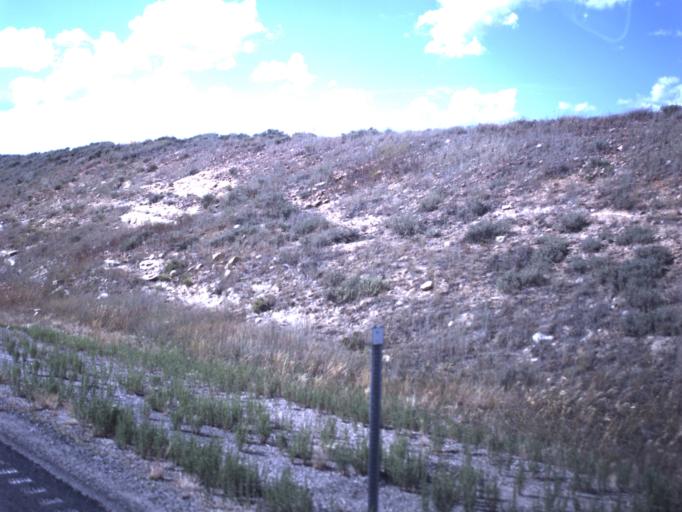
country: US
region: Utah
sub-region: Wasatch County
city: Heber
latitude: 40.1918
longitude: -111.0807
